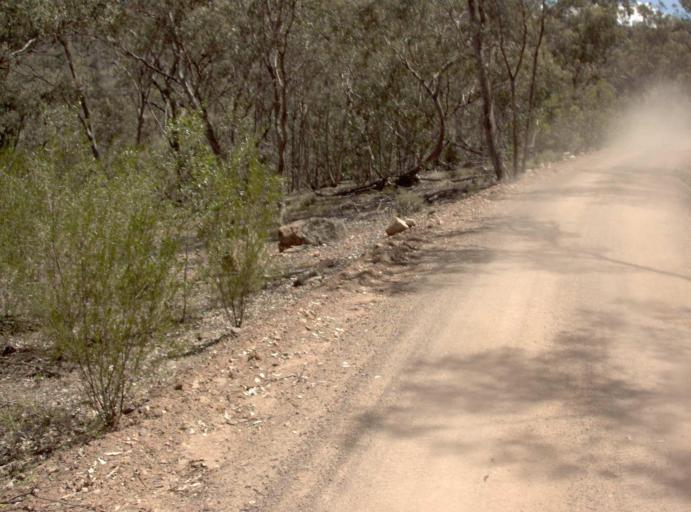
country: AU
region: New South Wales
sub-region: Snowy River
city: Jindabyne
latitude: -37.0905
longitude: 148.4111
